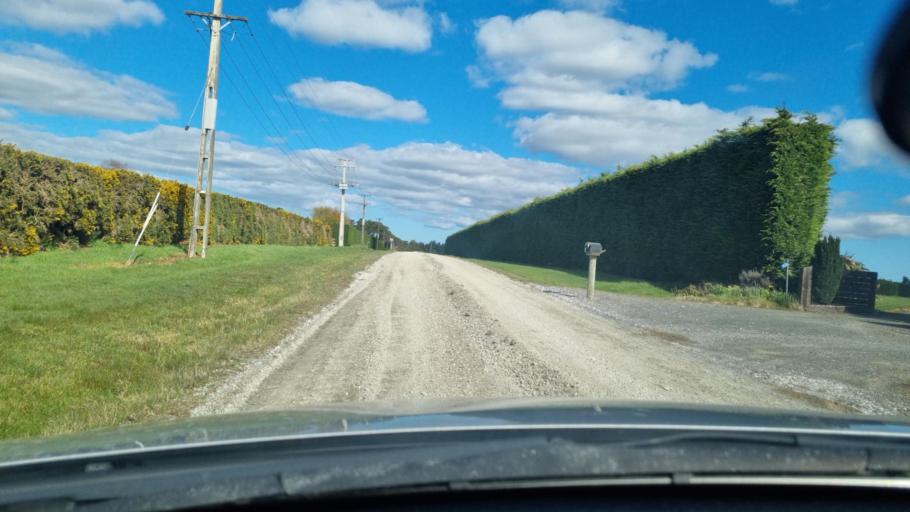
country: NZ
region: Southland
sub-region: Invercargill City
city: Invercargill
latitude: -46.4139
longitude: 168.4417
